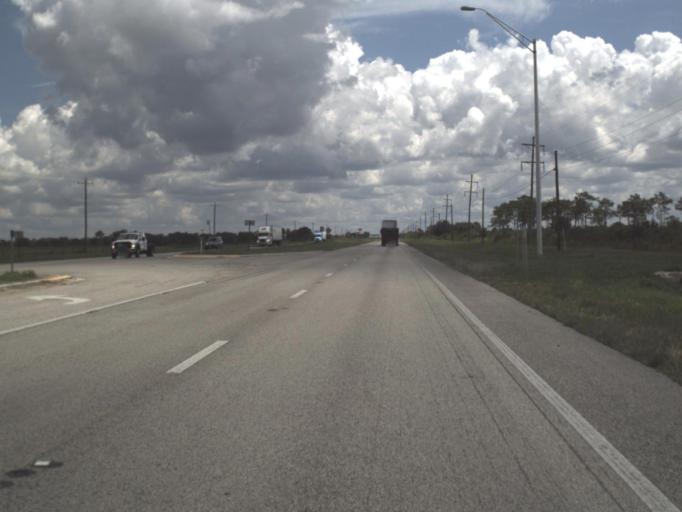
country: US
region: Florida
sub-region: Polk County
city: Babson Park
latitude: 27.8528
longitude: -81.3684
